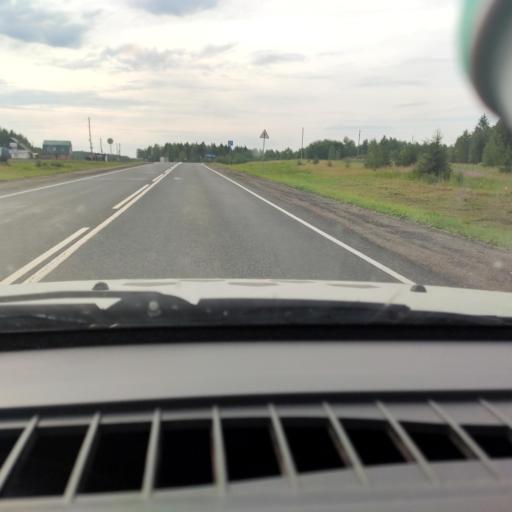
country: RU
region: Kirov
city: Kostino
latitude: 58.7180
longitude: 53.6725
